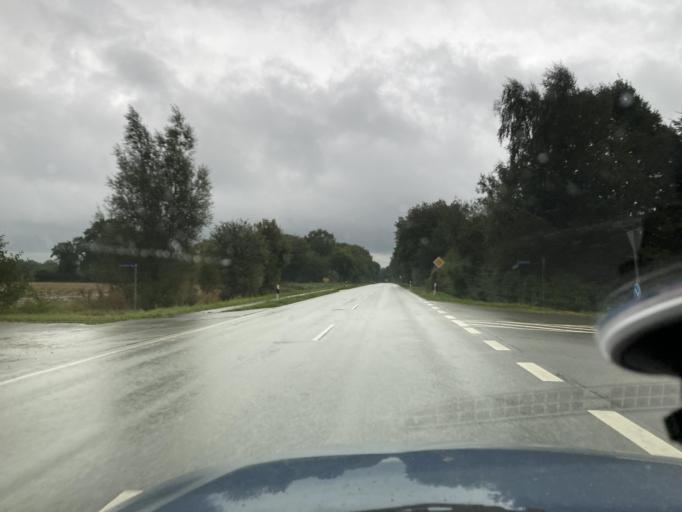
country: DE
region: Schleswig-Holstein
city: Dellstedt
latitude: 54.2175
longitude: 9.3699
